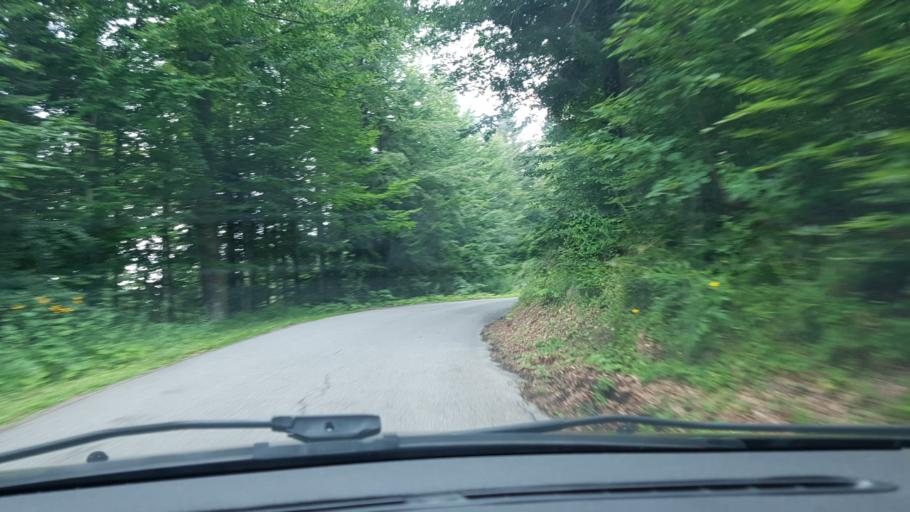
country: HR
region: Primorsko-Goranska
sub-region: Grad Delnice
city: Delnice
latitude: 45.3802
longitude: 14.6947
